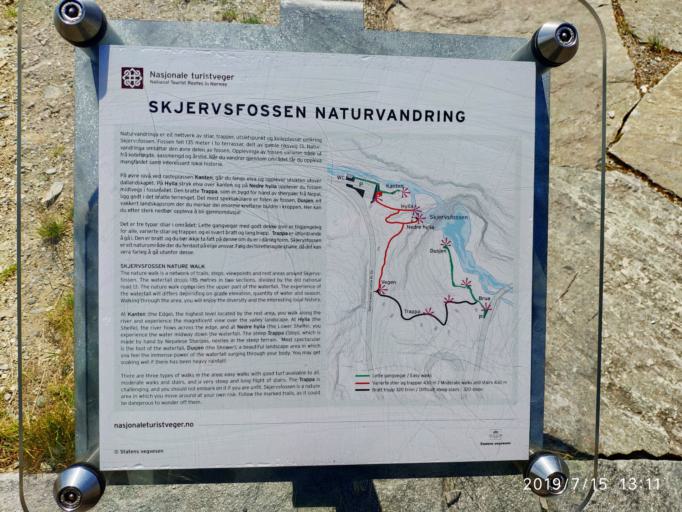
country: NO
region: Hordaland
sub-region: Granvin
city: Granvin
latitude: 60.5882
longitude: 6.6349
